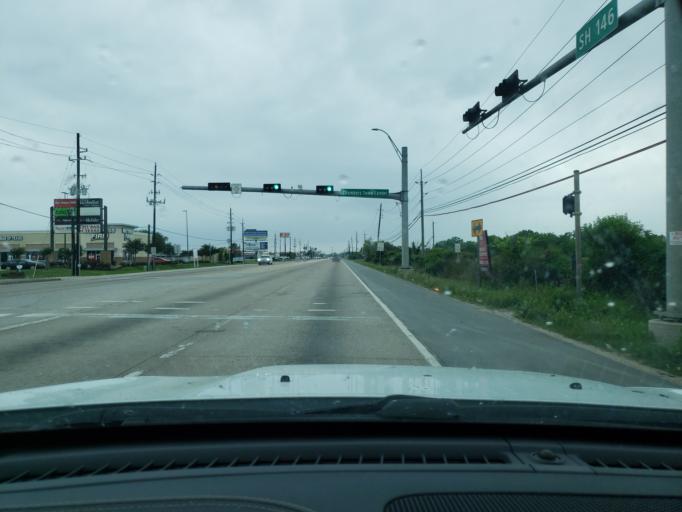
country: US
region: Texas
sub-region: Chambers County
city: Mont Belvieu
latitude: 29.8178
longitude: -94.9003
